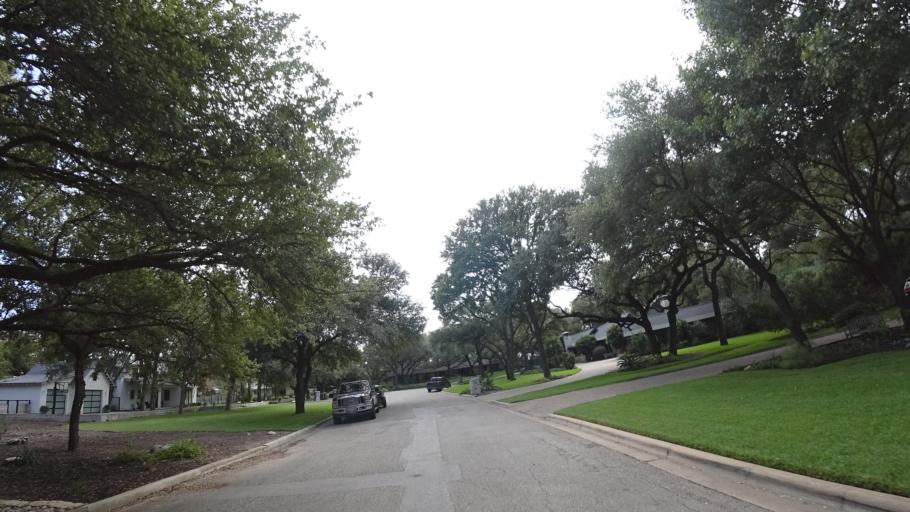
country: US
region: Texas
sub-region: Travis County
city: Rollingwood
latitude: 30.2817
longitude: -97.8053
